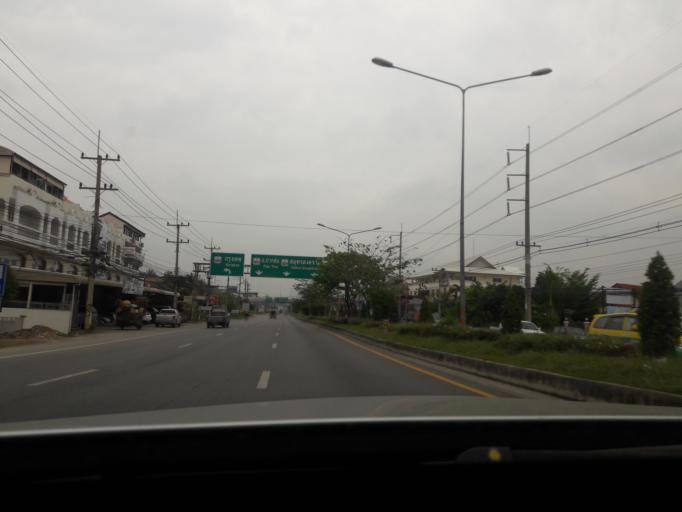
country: TH
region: Samut Songkhram
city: Samut Songkhram
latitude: 13.4211
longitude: 99.9894
